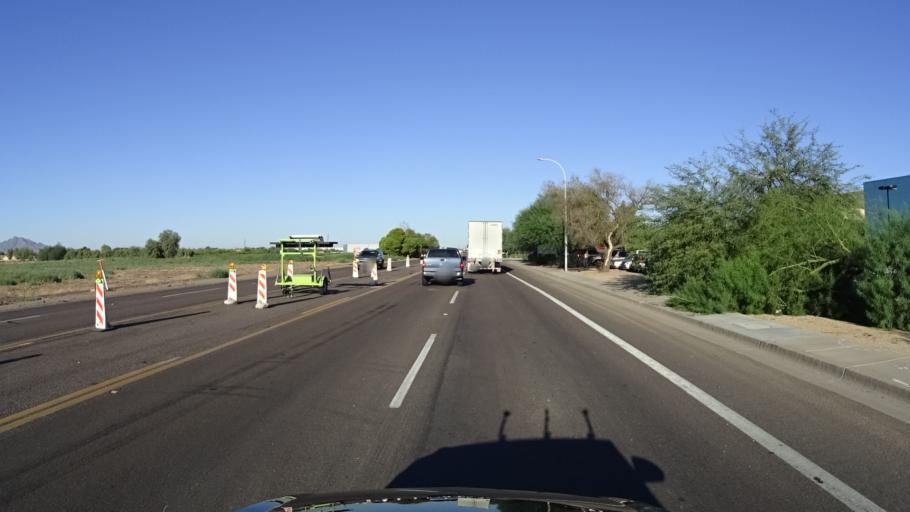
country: US
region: Arizona
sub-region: Maricopa County
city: Tolleson
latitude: 33.4372
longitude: -112.2310
